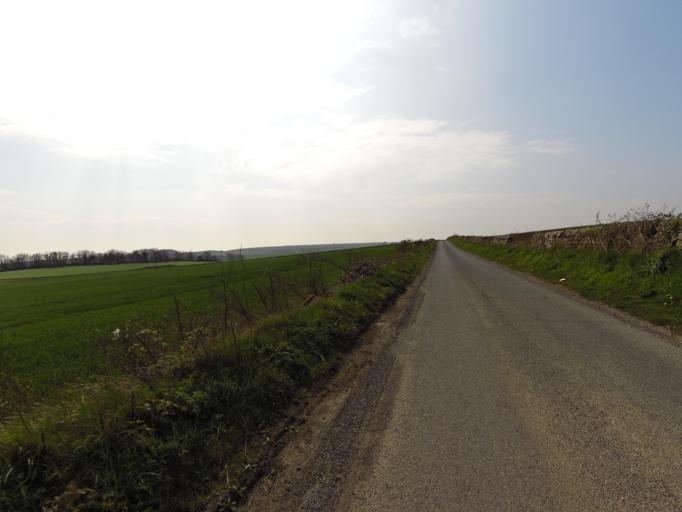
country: GB
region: Scotland
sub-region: Fife
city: Kinghorn
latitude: 56.0927
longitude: -3.1732
